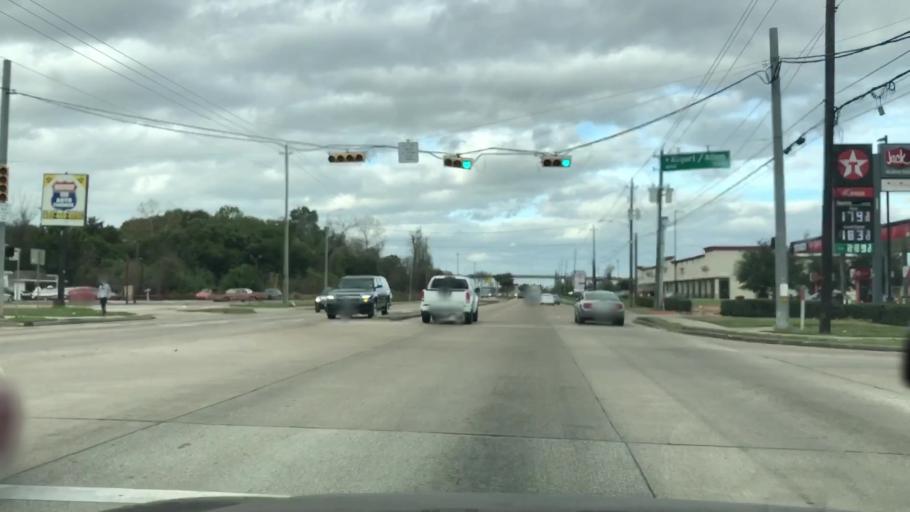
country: US
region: Texas
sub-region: Harris County
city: Bellaire
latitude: 29.6406
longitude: -95.4636
